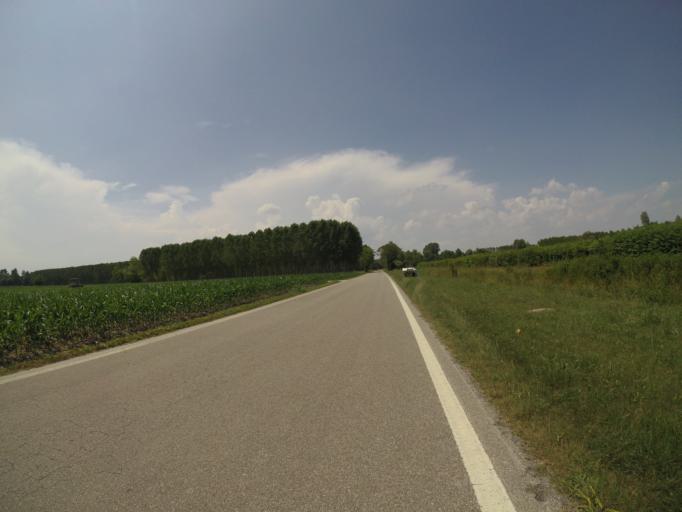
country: IT
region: Friuli Venezia Giulia
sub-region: Provincia di Udine
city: Rivignano
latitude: 45.8949
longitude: 13.0478
